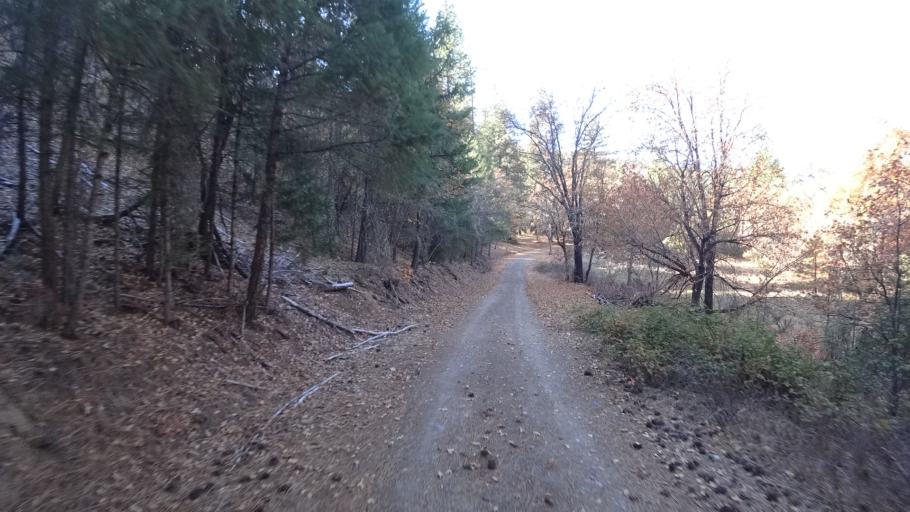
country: US
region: California
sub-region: Siskiyou County
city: Yreka
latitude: 41.8623
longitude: -122.7309
